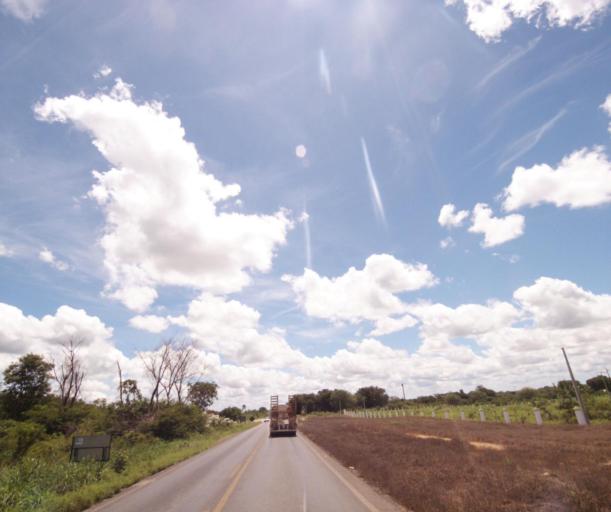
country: BR
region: Bahia
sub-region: Bom Jesus Da Lapa
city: Bom Jesus da Lapa
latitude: -13.2631
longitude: -43.5489
